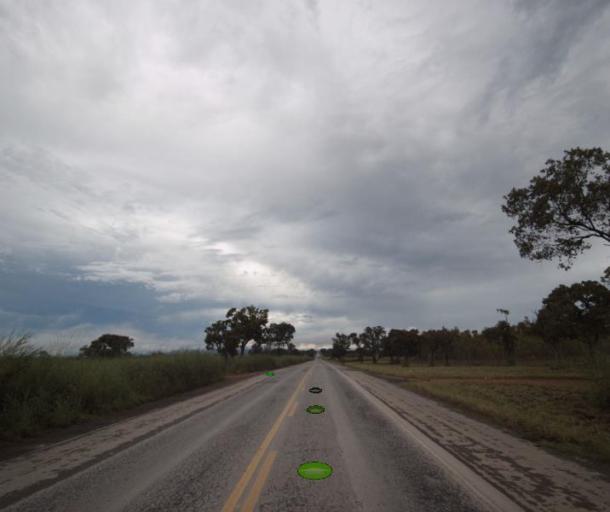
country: BR
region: Goias
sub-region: Porangatu
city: Porangatu
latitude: -13.5074
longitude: -49.1254
